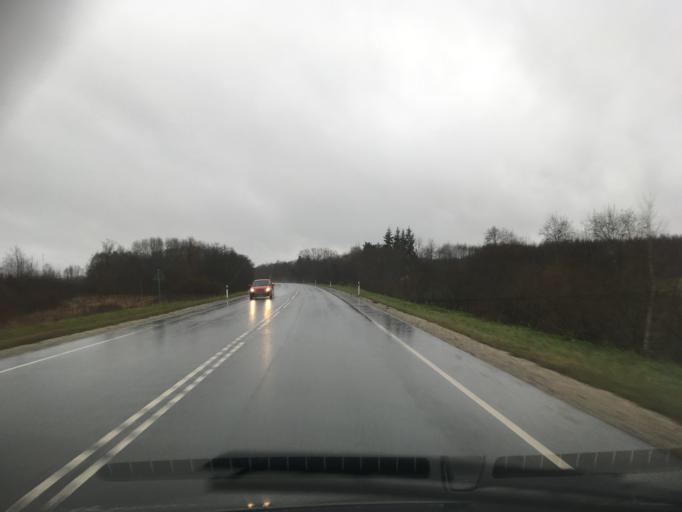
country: EE
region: Laeaene
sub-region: Lihula vald
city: Lihula
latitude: 58.8334
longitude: 24.0549
